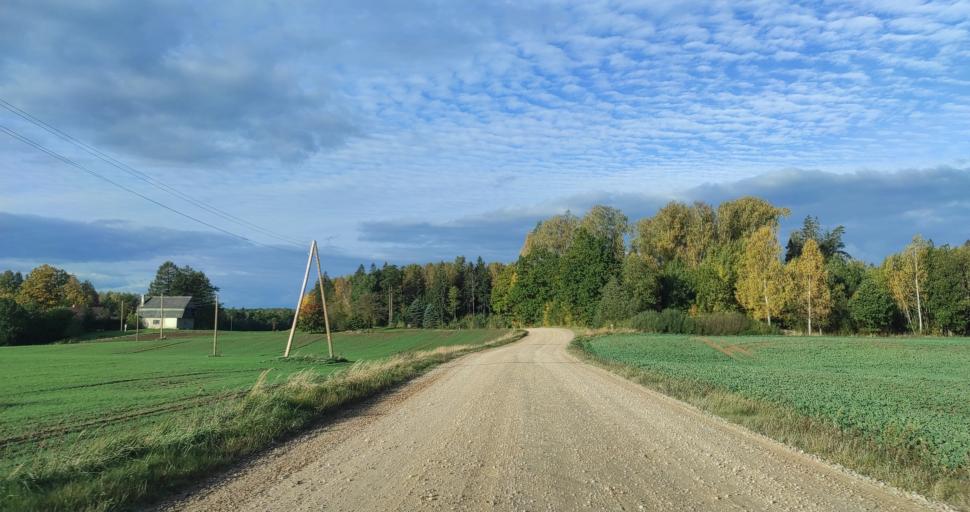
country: LV
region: Skrunda
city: Skrunda
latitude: 56.7477
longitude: 21.8315
